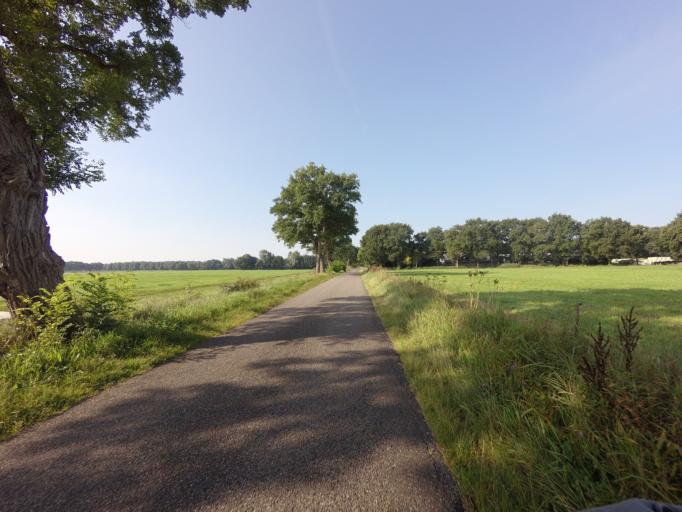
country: NL
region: Friesland
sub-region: Gemeente Weststellingwerf
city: Steggerda
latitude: 52.8983
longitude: 6.0912
